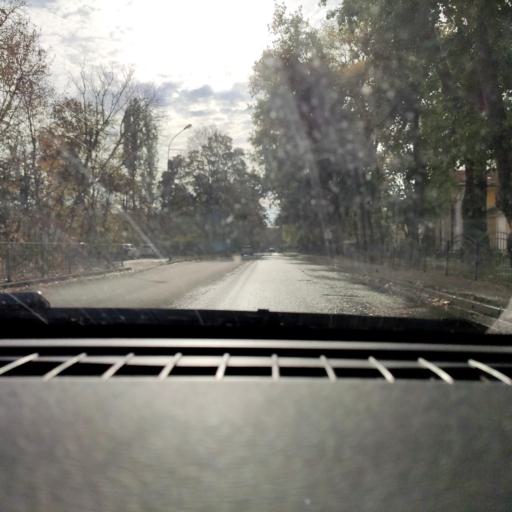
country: RU
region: Voronezj
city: Voronezh
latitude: 51.7161
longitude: 39.2222
